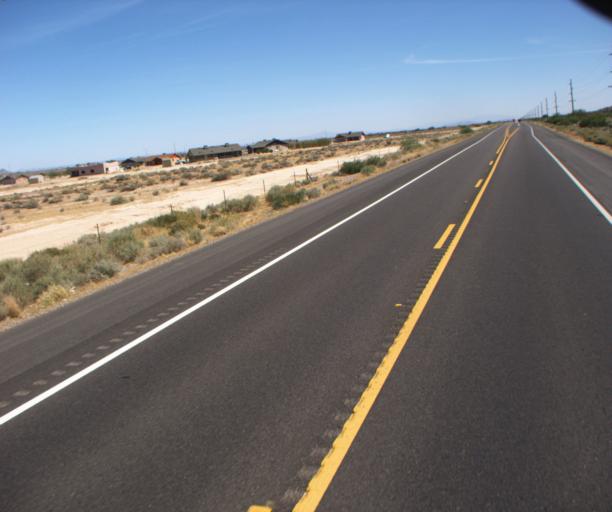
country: US
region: Arizona
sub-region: Pinal County
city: Sacaton
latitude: 33.0544
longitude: -111.6796
